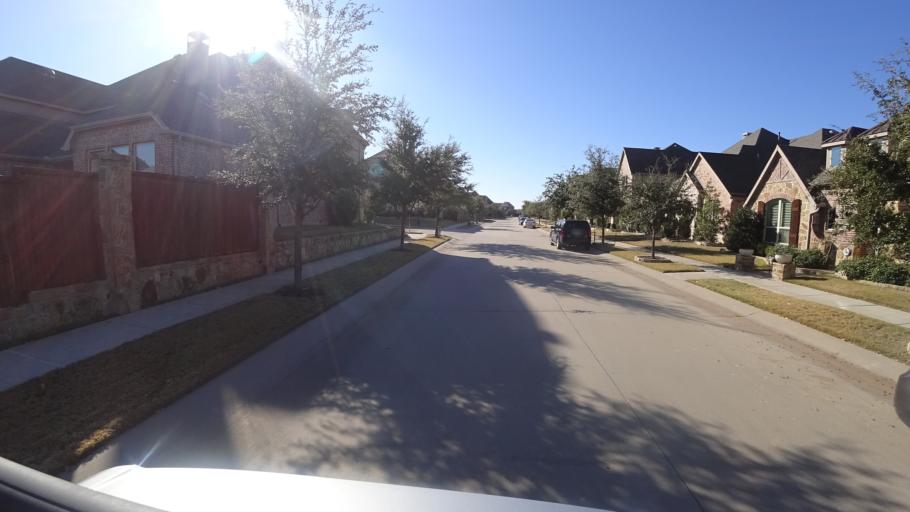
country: US
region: Texas
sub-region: Denton County
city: The Colony
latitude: 33.0400
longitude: -96.9216
